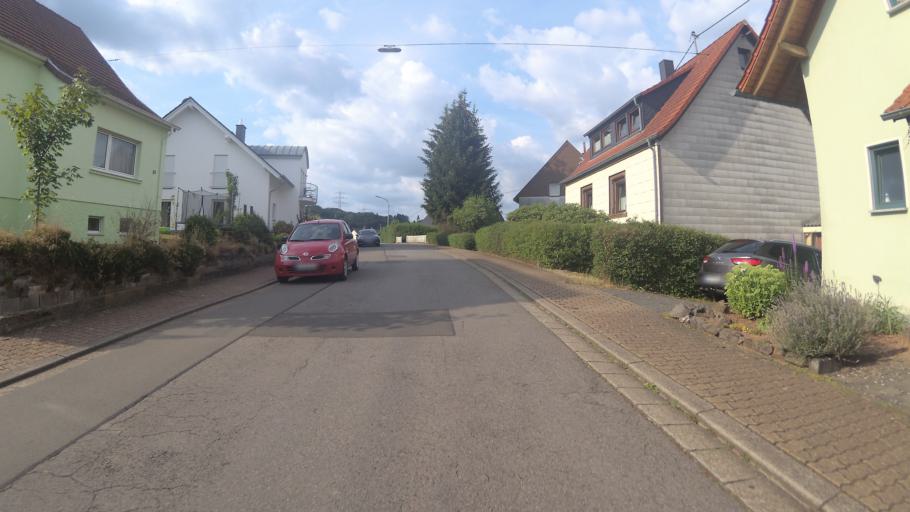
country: DE
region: Saarland
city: Illingen
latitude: 49.3760
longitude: 7.0124
